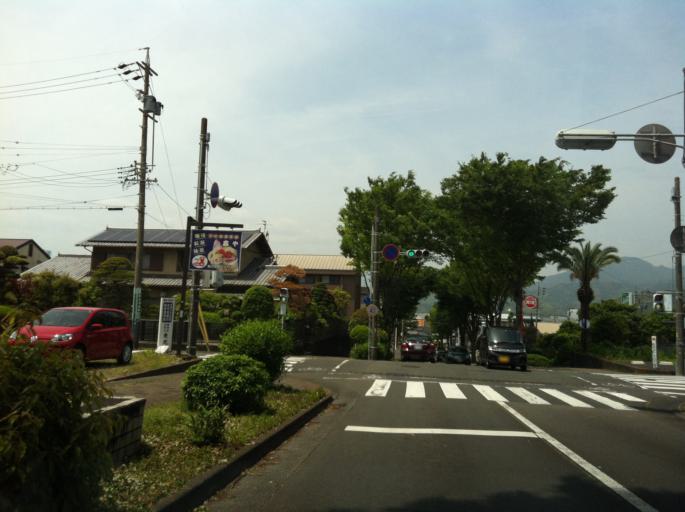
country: JP
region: Shizuoka
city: Shizuoka-shi
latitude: 34.9961
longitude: 138.4391
